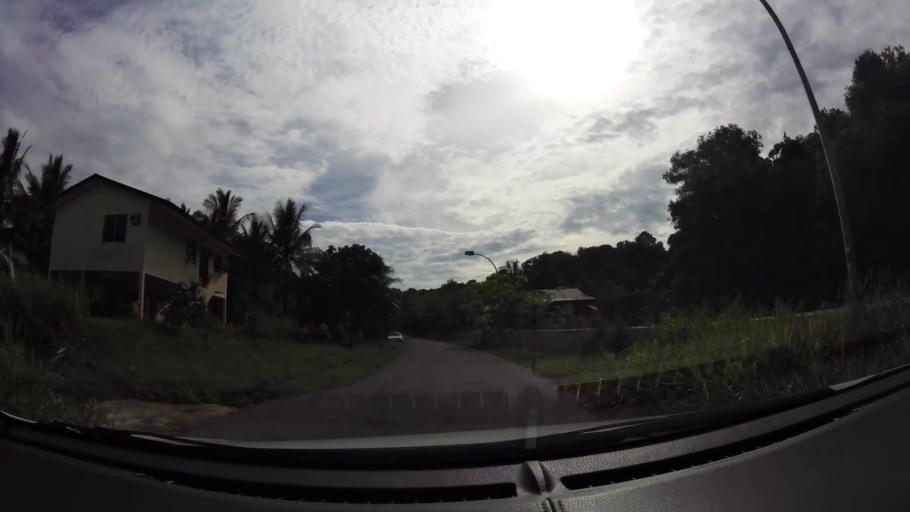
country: BN
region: Brunei and Muara
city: Bandar Seri Begawan
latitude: 4.8961
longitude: 114.8853
